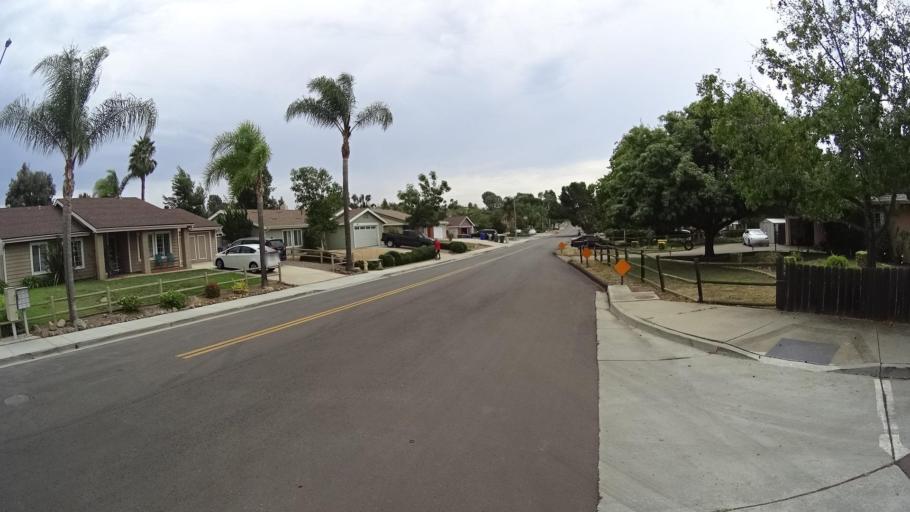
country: US
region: California
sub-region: San Diego County
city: Escondido
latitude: 33.1482
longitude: -117.1159
